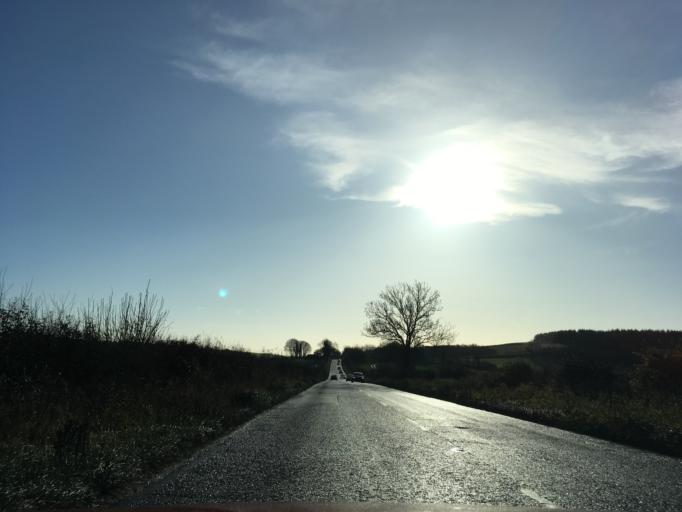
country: GB
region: England
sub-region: Wiltshire
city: Collingbourne Kingston
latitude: 51.3148
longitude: -1.6659
